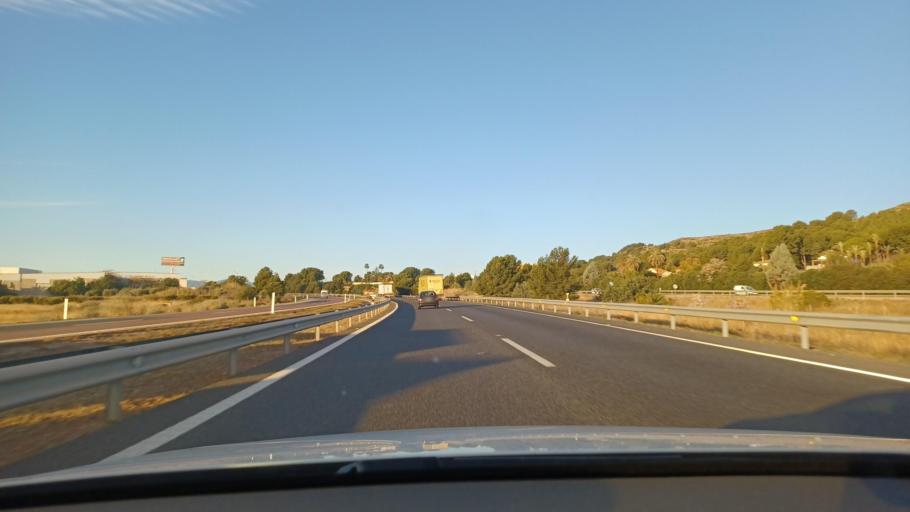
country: ES
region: Valencia
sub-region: Provincia de Castello
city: Castello de la Plana
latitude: 40.0050
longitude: -0.0601
